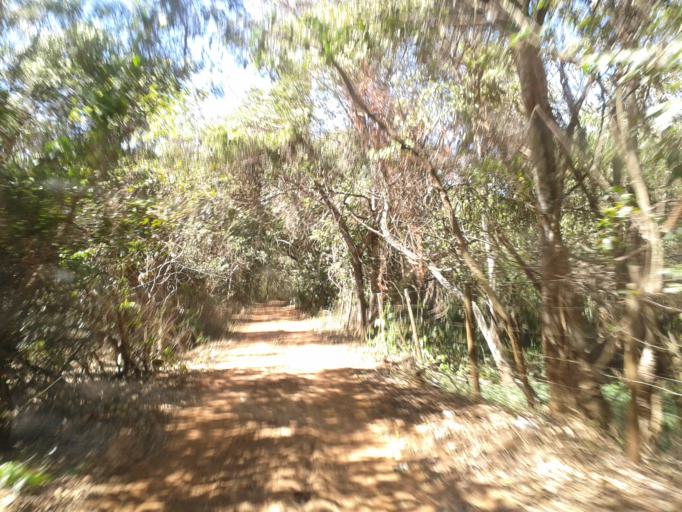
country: BR
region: Minas Gerais
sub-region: Monte Alegre De Minas
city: Monte Alegre de Minas
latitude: -18.8246
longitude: -49.1122
